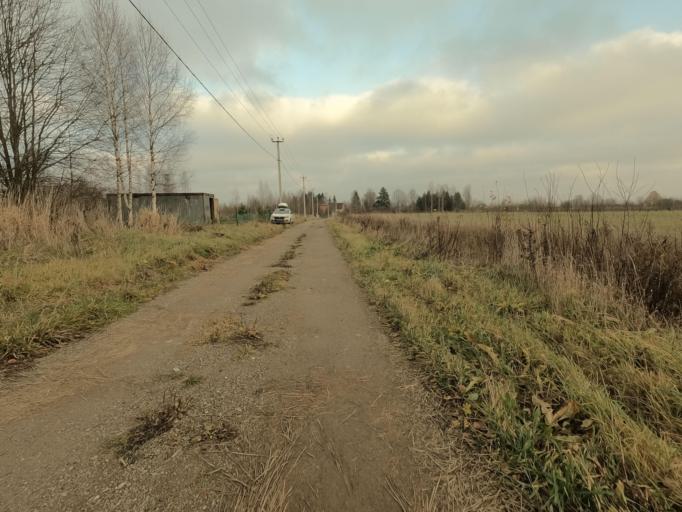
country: RU
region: Leningrad
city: Mga
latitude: 59.7550
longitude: 31.0603
